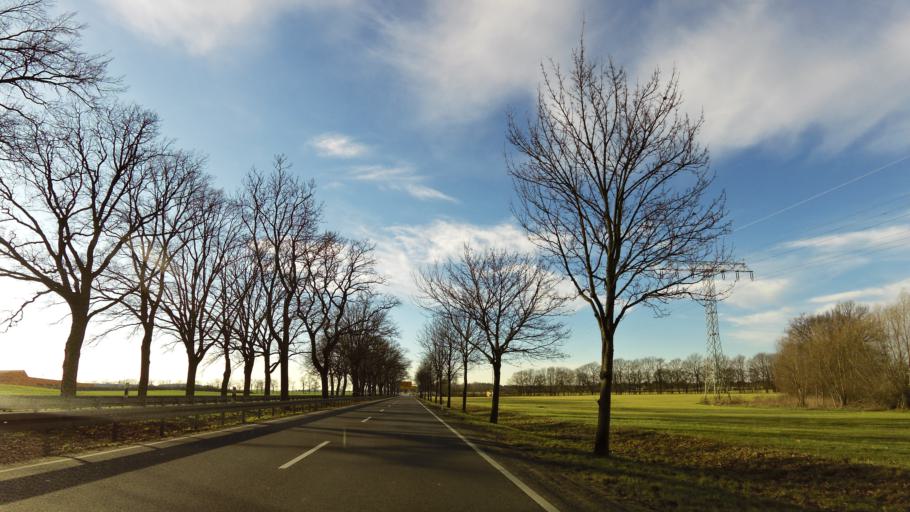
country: DE
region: Brandenburg
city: Schoneiche
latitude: 52.5009
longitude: 13.7095
